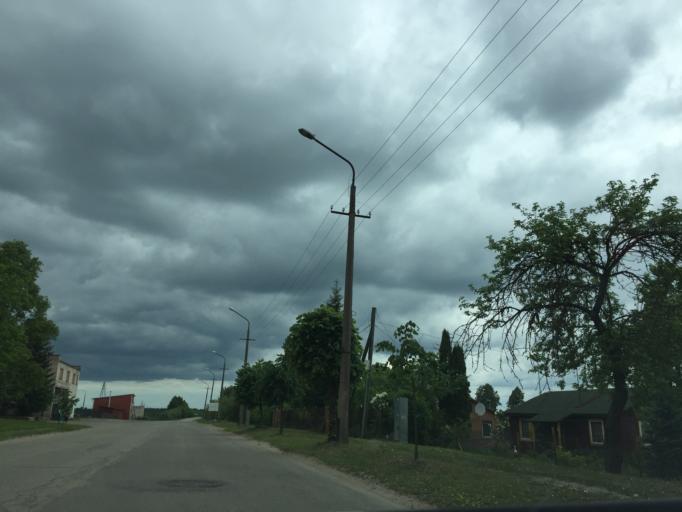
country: LV
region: Dagda
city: Dagda
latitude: 56.0983
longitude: 27.5219
